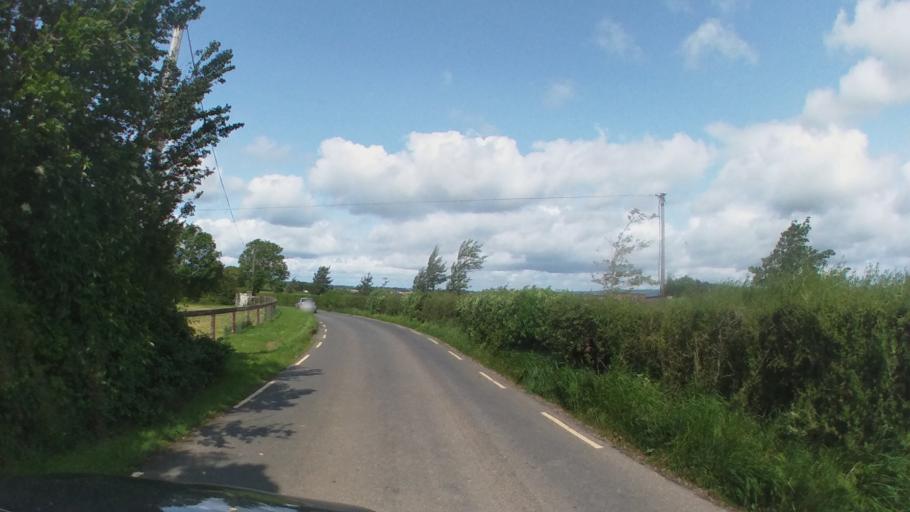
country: IE
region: Leinster
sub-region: Kilkenny
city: Graiguenamanagh
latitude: 52.6048
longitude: -6.9965
